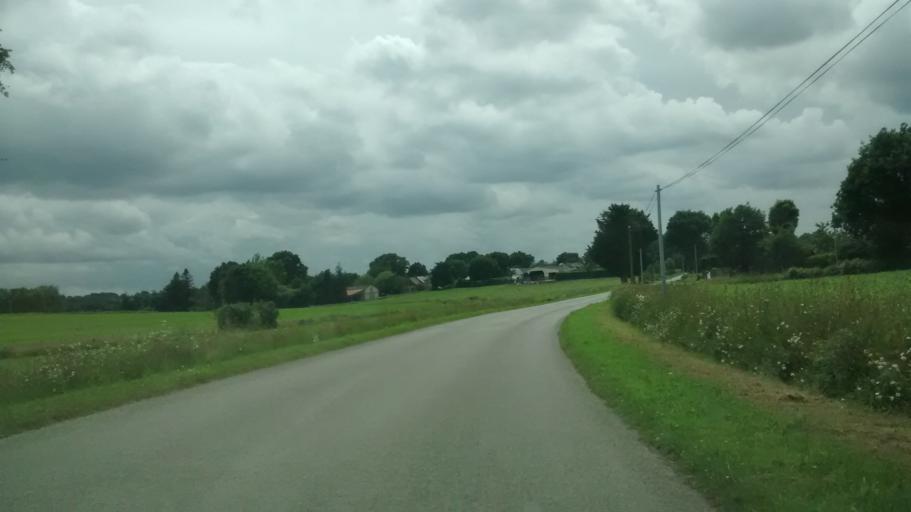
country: FR
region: Brittany
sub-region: Departement du Morbihan
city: Ruffiac
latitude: 47.8345
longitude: -2.2249
